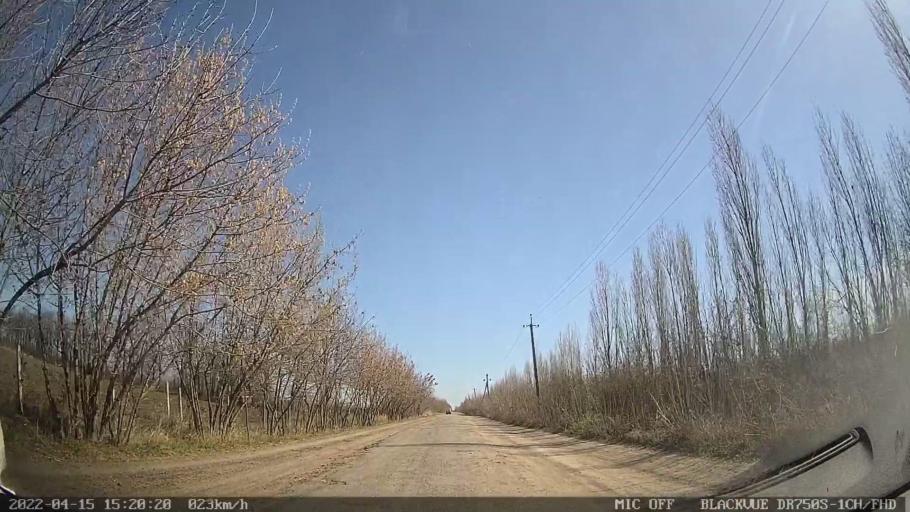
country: MD
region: Raionul Ocnita
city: Otaci
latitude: 48.3861
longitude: 27.9077
